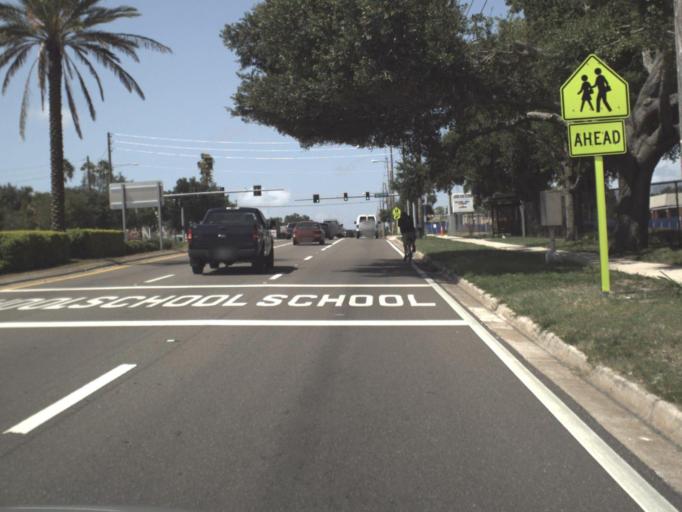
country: US
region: Florida
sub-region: Pinellas County
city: Largo
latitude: 27.9192
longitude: -82.7876
